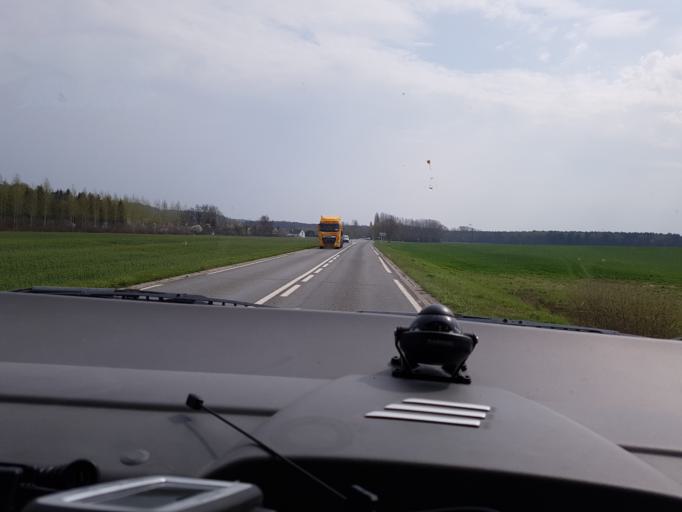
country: FR
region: Picardie
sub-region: Departement de l'Aisne
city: Coucy-le-Chateau-Auffrique
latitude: 49.5140
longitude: 3.3088
